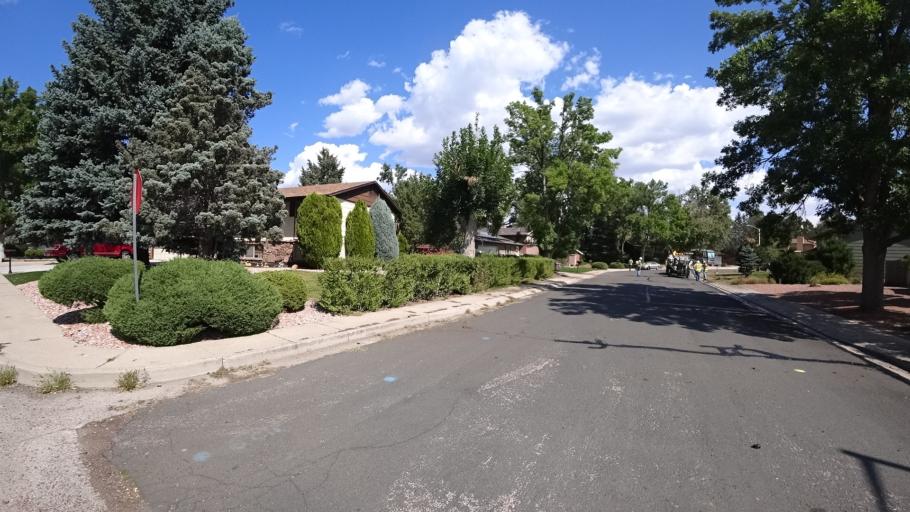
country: US
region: Colorado
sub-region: El Paso County
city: Cimarron Hills
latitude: 38.8769
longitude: -104.7489
